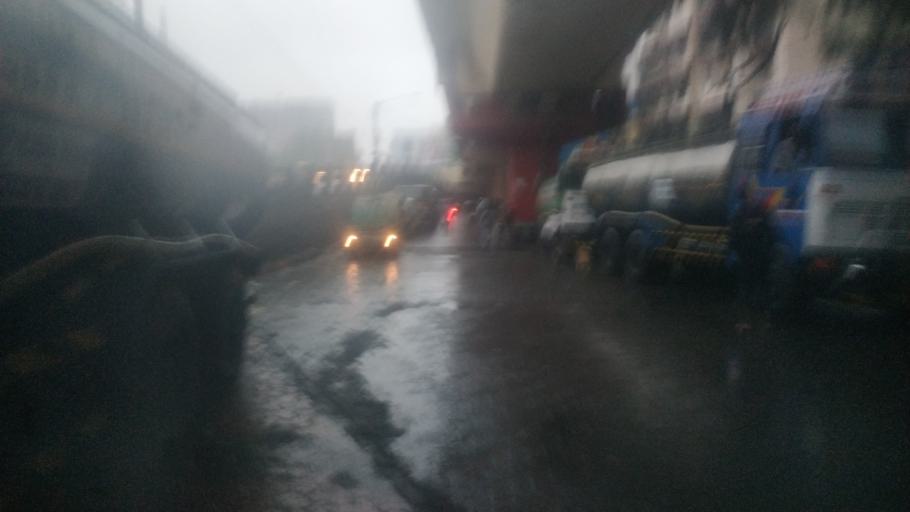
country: IN
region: Maharashtra
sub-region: Mumbai Suburban
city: Mumbai
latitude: 19.1161
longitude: 72.8440
